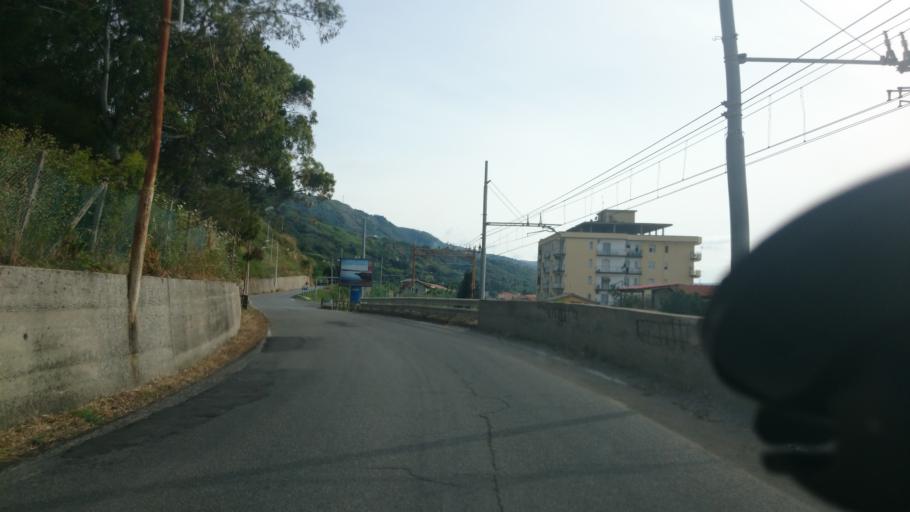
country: IT
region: Calabria
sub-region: Provincia di Vibo-Valentia
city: Maierato
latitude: 38.7307
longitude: 16.1550
